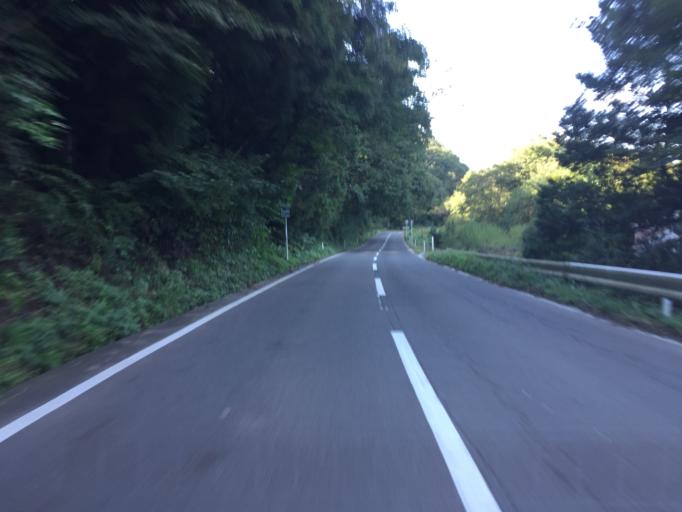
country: JP
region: Miyagi
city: Marumori
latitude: 37.8725
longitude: 140.7821
